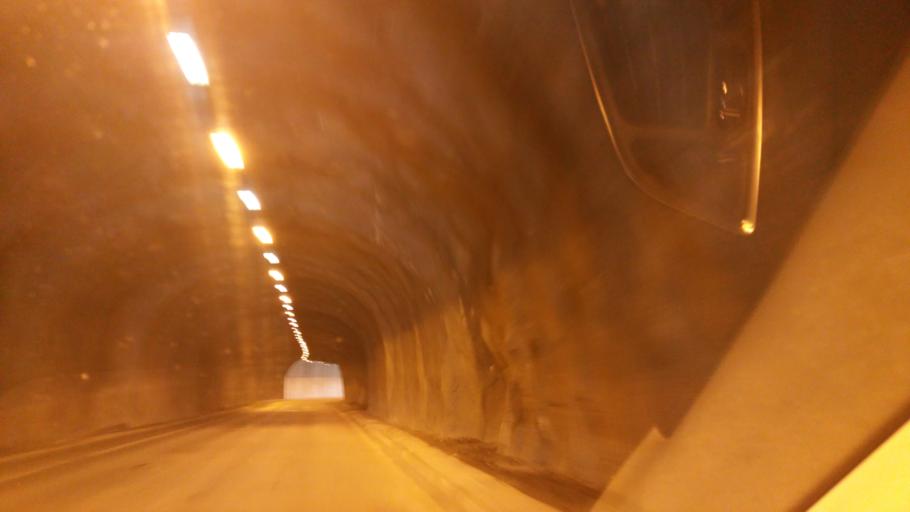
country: FR
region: Rhone-Alpes
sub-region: Departement de la Savoie
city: Saint-Jean-de-Maurienne
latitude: 45.2172
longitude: 6.3057
